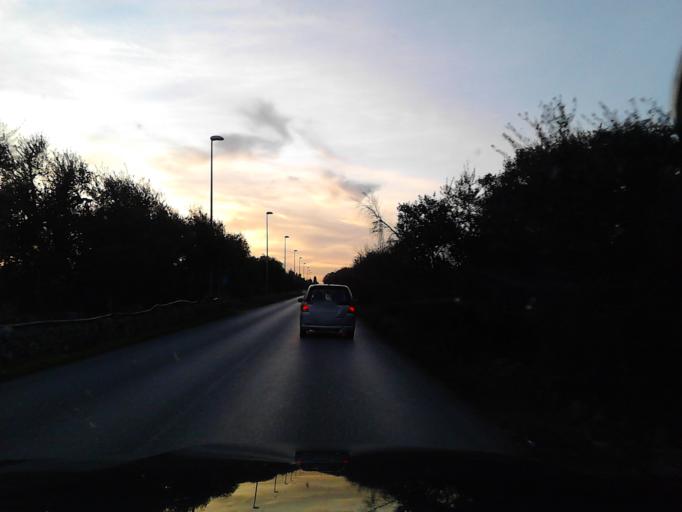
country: IT
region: Apulia
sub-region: Provincia di Bari
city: Capurso
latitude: 41.0467
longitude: 16.9073
